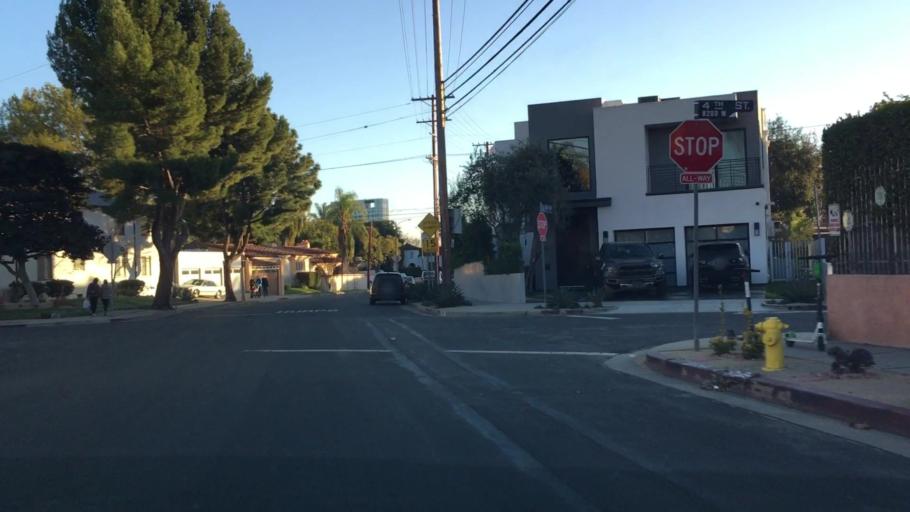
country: US
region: California
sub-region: Los Angeles County
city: West Hollywood
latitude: 34.0708
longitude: -118.3675
